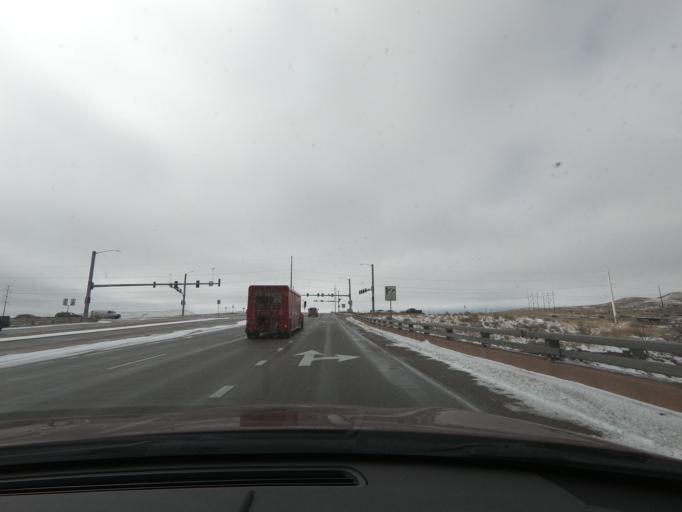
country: US
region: Colorado
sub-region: El Paso County
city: Security-Widefield
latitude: 38.7260
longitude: -104.7307
